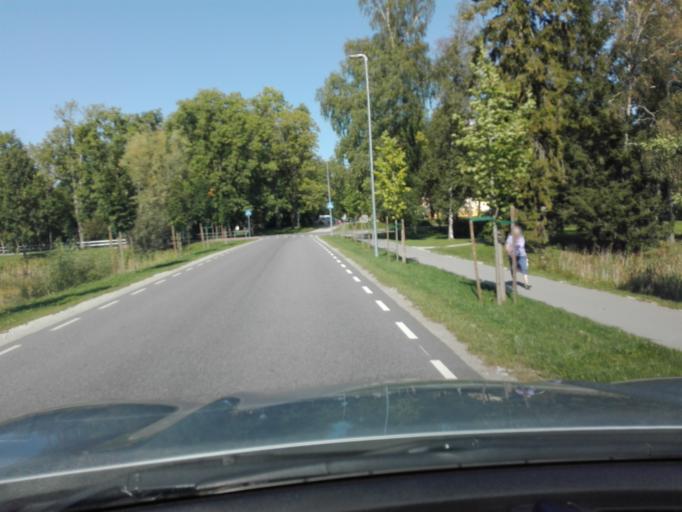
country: EE
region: Raplamaa
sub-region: Rapla vald
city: Rapla
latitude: 59.0220
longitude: 24.7644
